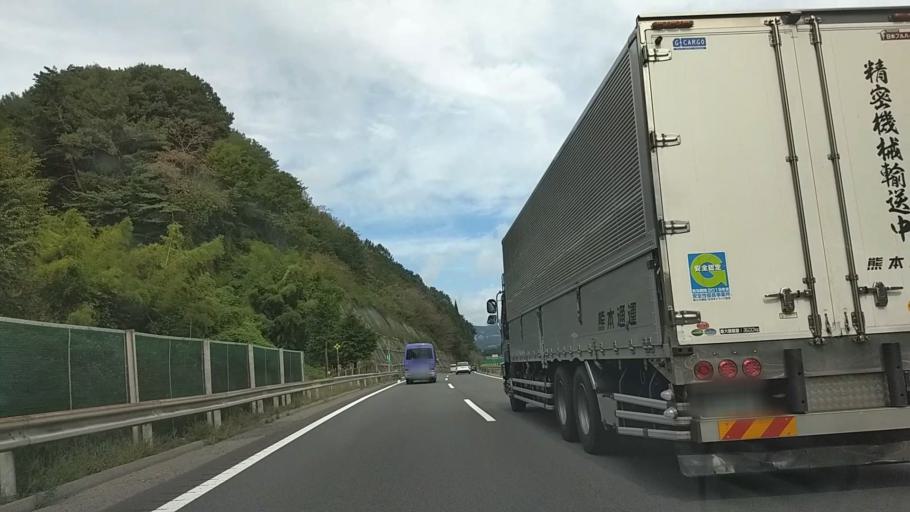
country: JP
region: Nagano
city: Okaya
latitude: 36.0333
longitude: 138.0658
